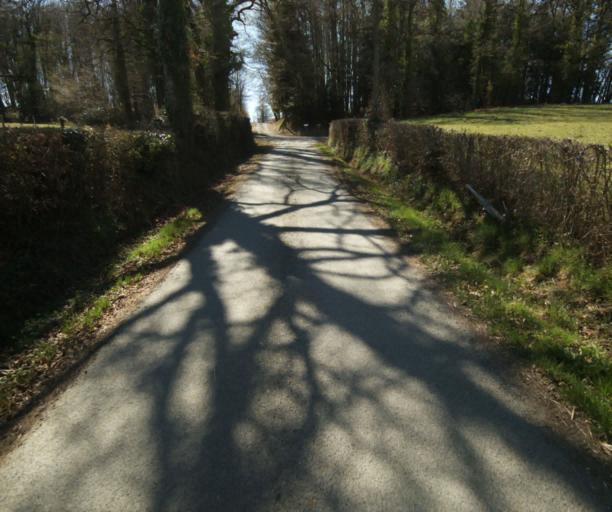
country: FR
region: Limousin
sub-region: Departement de la Correze
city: Saint-Clement
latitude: 45.3973
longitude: 1.6401
